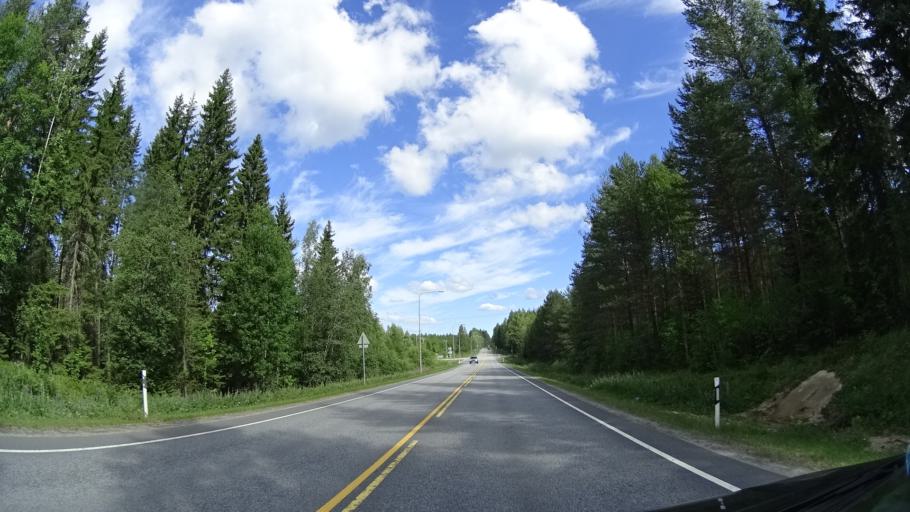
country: FI
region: Pirkanmaa
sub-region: Luoteis-Pirkanmaa
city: Kihnioe
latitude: 62.1886
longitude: 23.1720
